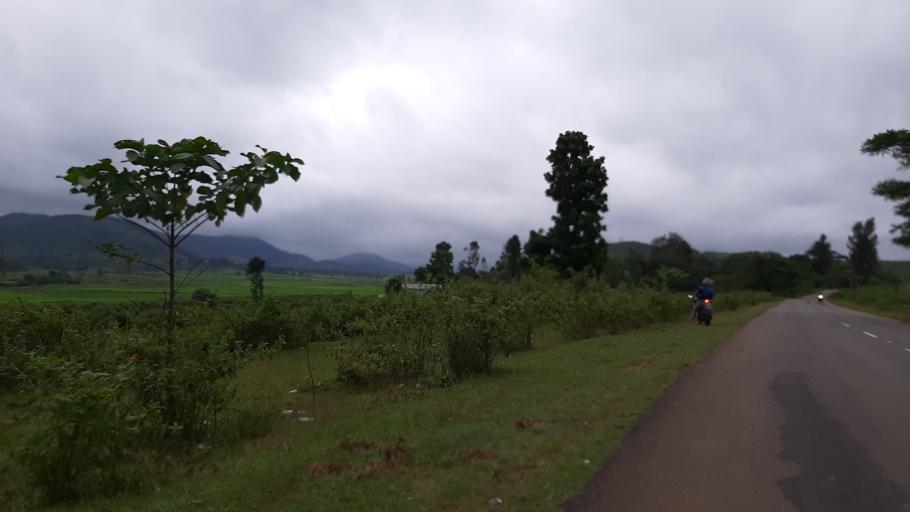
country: IN
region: Andhra Pradesh
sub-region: Vizianagaram District
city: Salur
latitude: 18.2989
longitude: 82.9122
